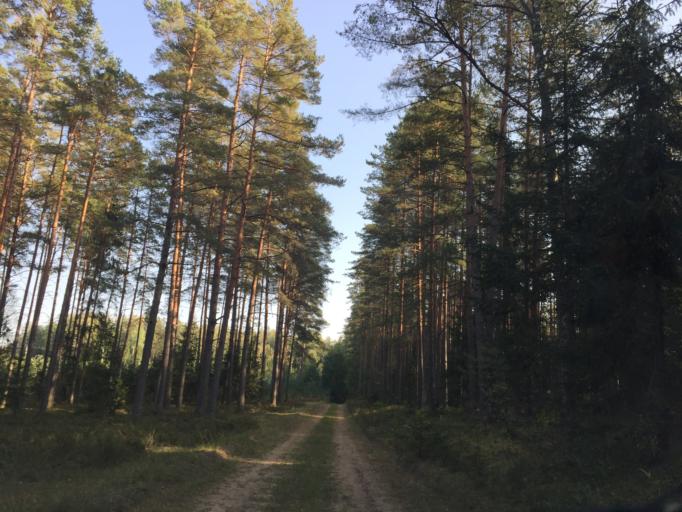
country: LV
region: Ogre
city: Ogre
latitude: 56.8450
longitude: 24.5826
